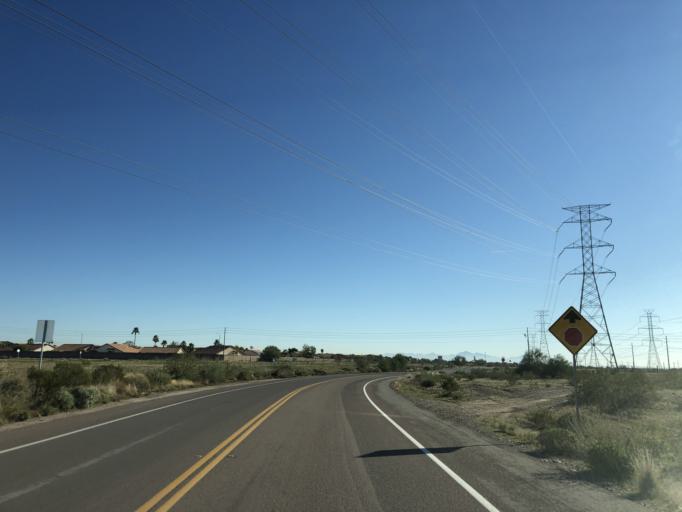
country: US
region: Arizona
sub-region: Maricopa County
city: Sun City West
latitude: 33.6760
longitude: -112.2994
